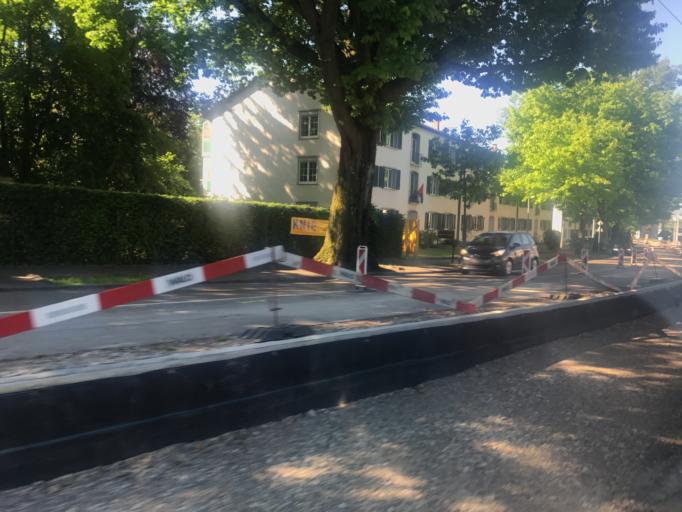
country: CH
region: Basel-City
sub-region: Basel-Stadt
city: Riehen
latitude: 47.5757
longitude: 7.6344
